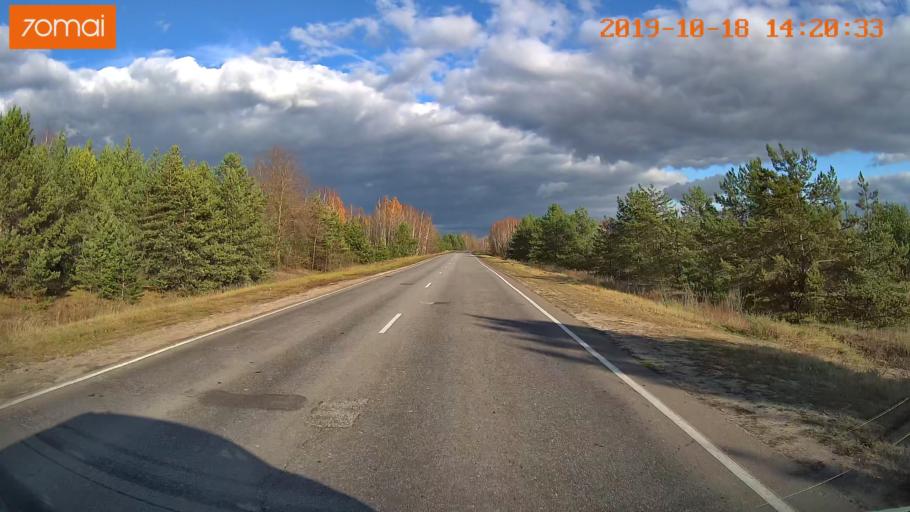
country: RU
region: Rjazan
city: Tuma
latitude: 55.1455
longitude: 40.4348
